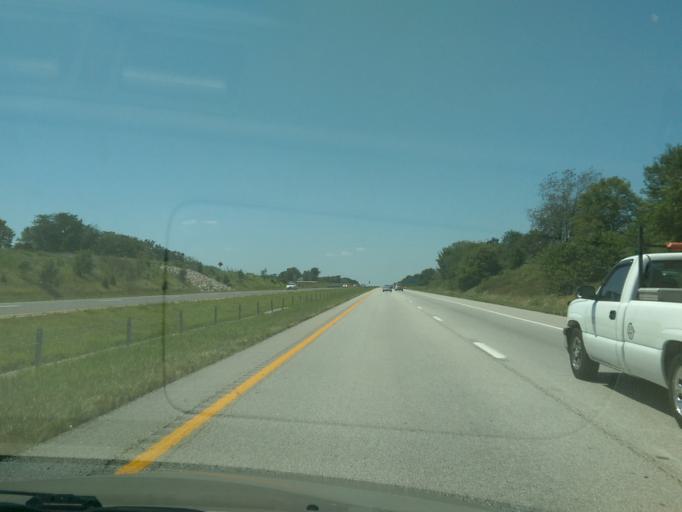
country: US
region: Missouri
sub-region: Saline County
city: Marshall
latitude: 38.9503
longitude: -93.0456
